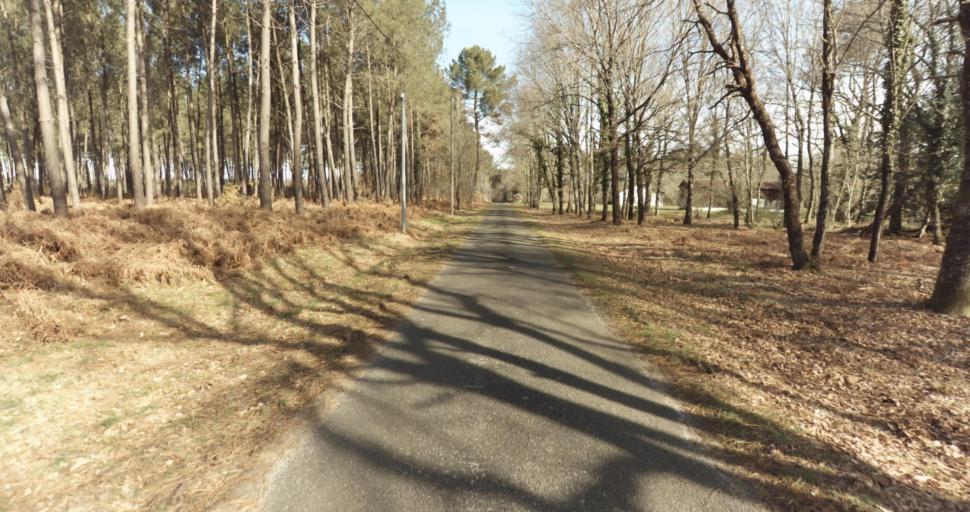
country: FR
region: Aquitaine
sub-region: Departement des Landes
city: Roquefort
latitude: 44.1082
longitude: -0.3137
